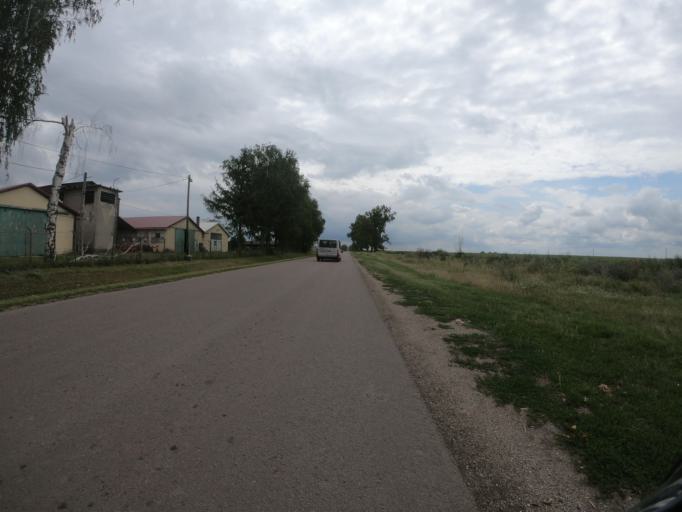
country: HU
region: Borsod-Abauj-Zemplen
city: Szentistvan
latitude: 47.7664
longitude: 20.6719
